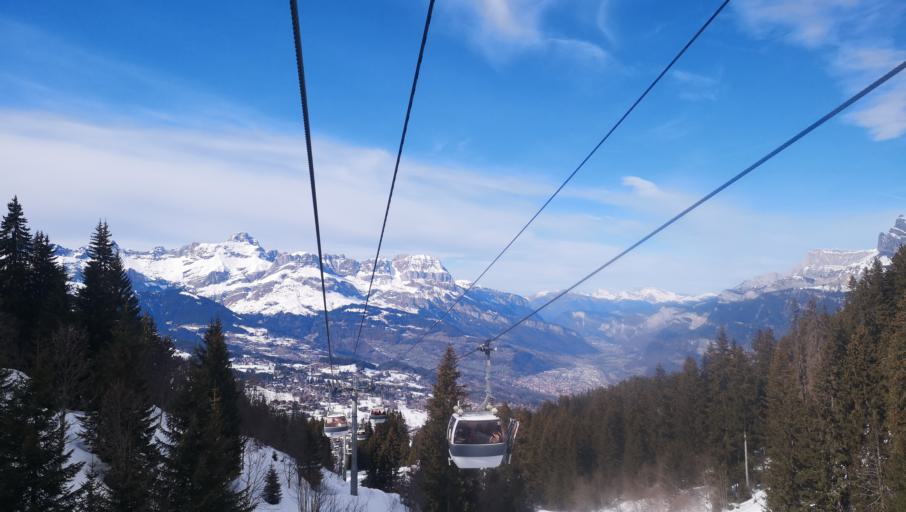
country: FR
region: Rhone-Alpes
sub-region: Departement de la Haute-Savoie
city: Combloux
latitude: 45.8648
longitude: 6.6571
